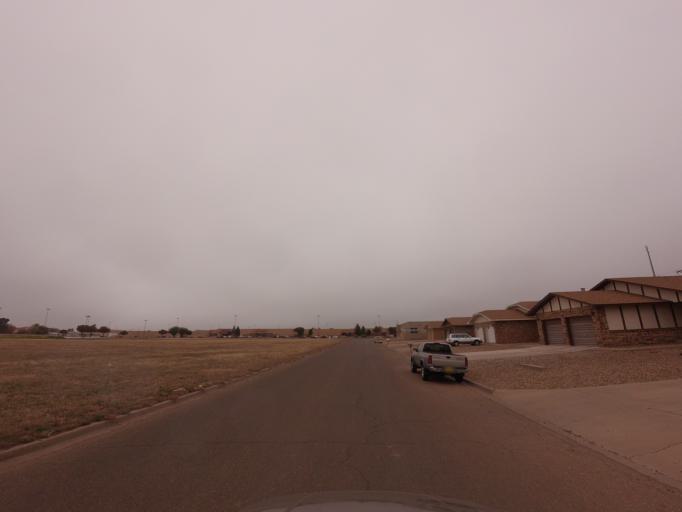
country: US
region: New Mexico
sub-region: Curry County
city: Clovis
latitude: 34.4262
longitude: -103.1901
